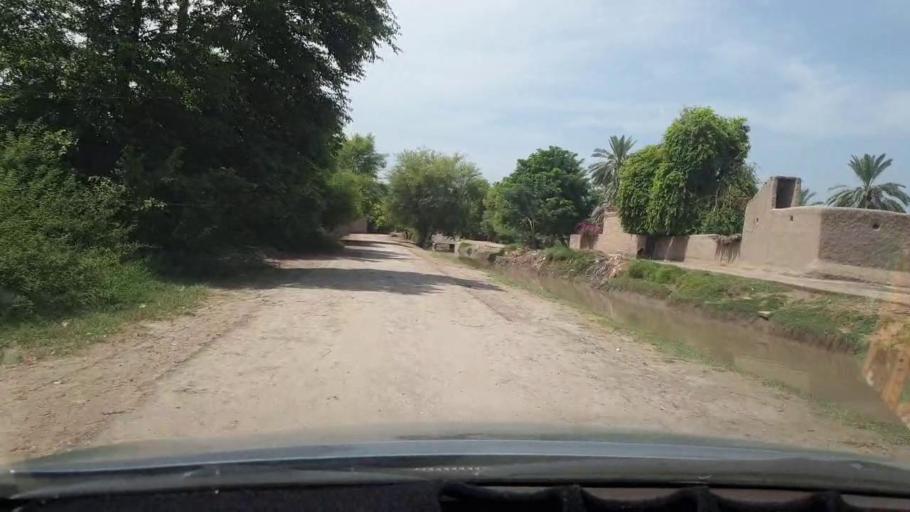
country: PK
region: Sindh
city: Khairpur
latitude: 27.4947
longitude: 68.7451
